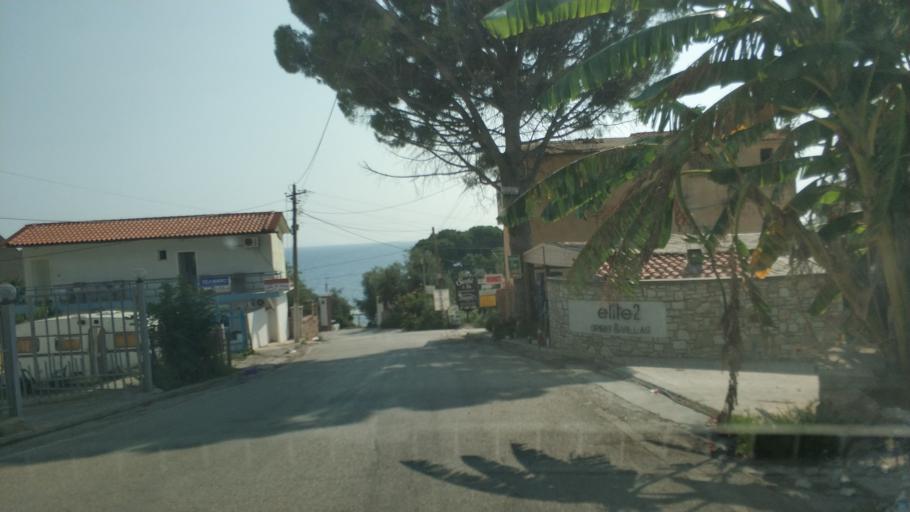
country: AL
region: Vlore
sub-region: Rrethi i Vlores
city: Vranisht
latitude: 40.1456
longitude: 19.6340
